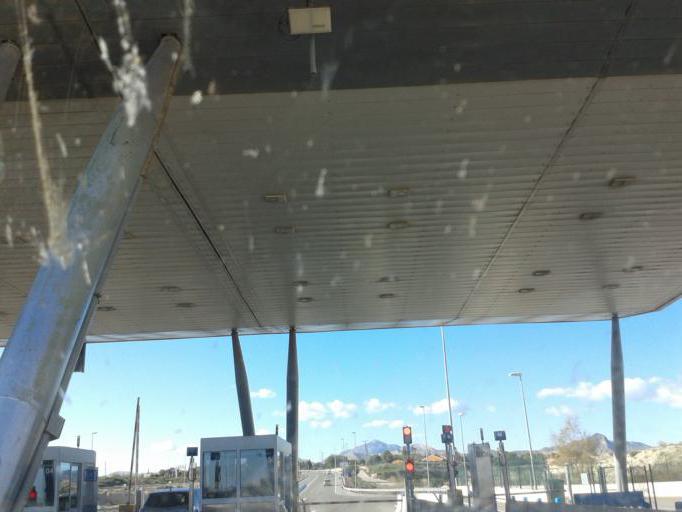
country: ES
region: Valencia
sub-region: Provincia de Alicante
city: Muchamiel
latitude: 38.4399
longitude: -0.4548
